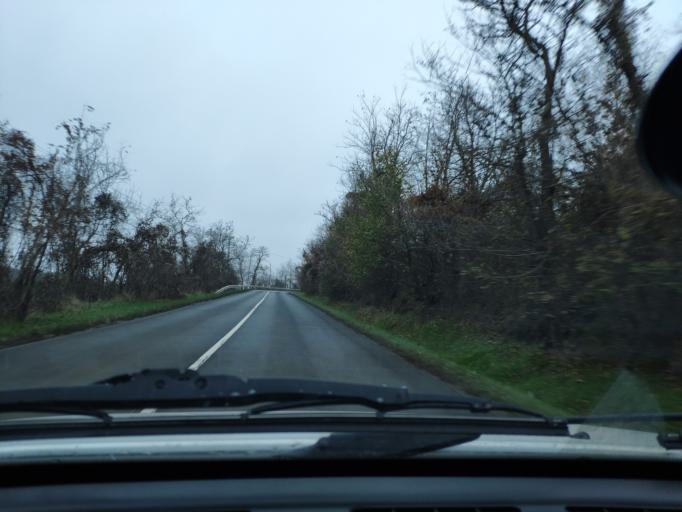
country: HU
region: Pest
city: Soskut
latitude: 47.4270
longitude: 18.8251
